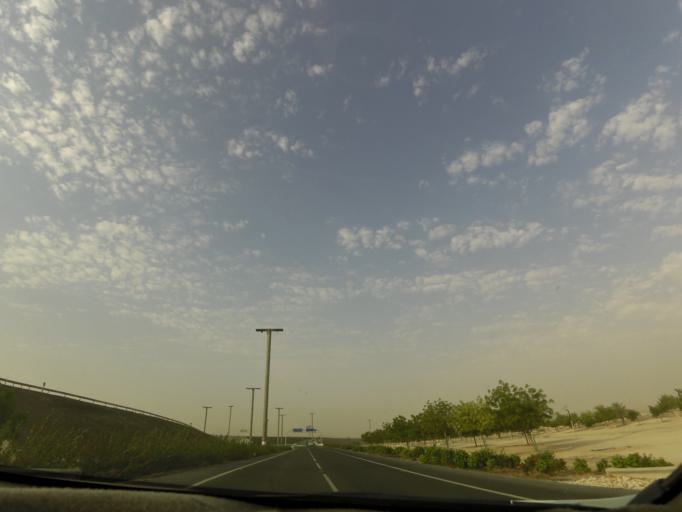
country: QA
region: Al Wakrah
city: Al Wakrah
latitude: 25.2420
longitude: 51.5898
